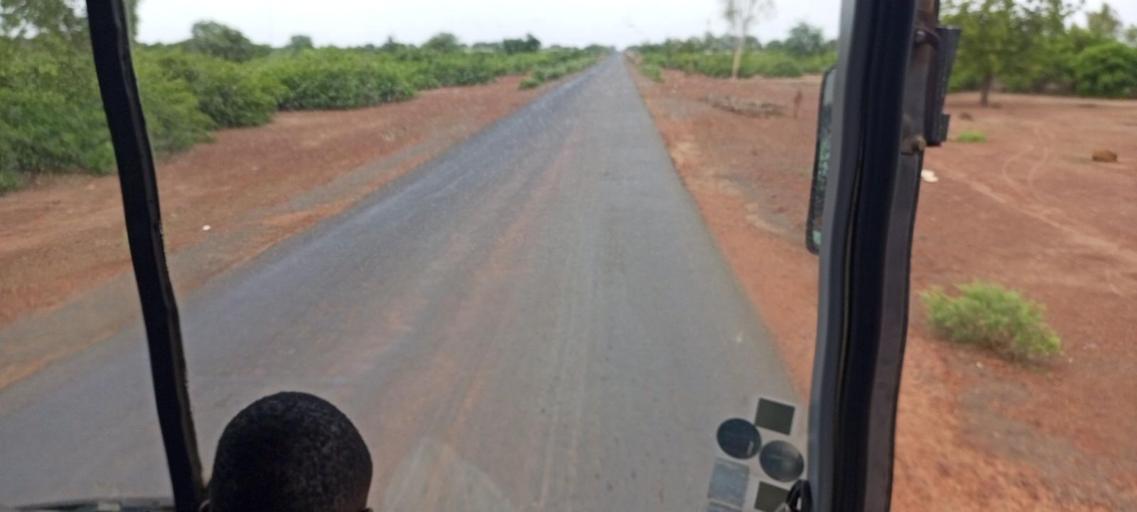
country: ML
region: Sikasso
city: Koutiala
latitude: 12.5431
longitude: -5.5776
